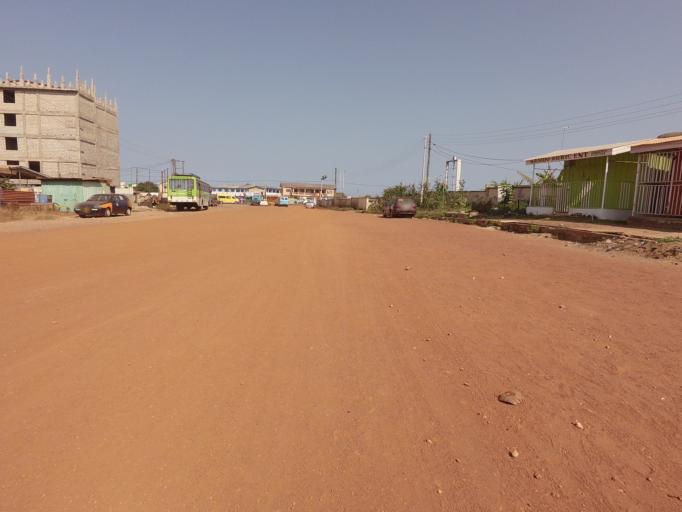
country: GH
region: Greater Accra
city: Teshi Old Town
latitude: 5.5773
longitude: -0.1117
